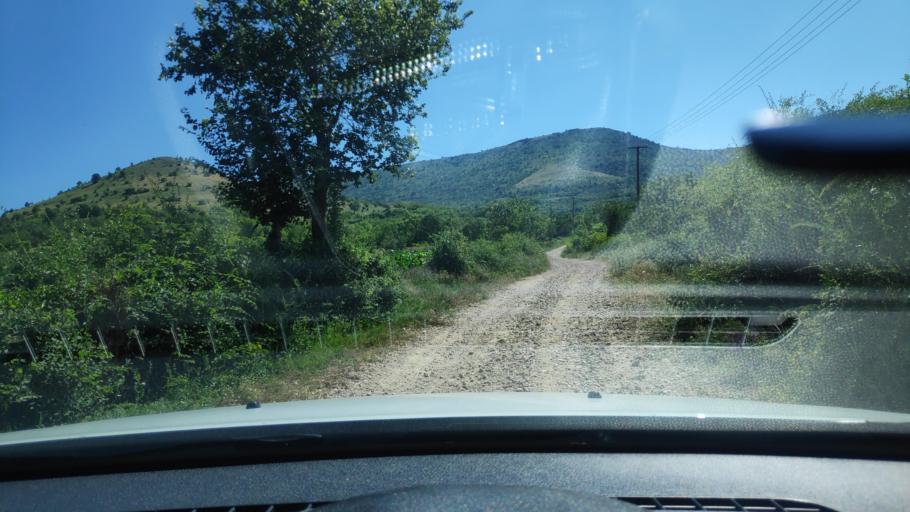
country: MK
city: Klechovce
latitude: 42.0726
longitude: 21.8944
